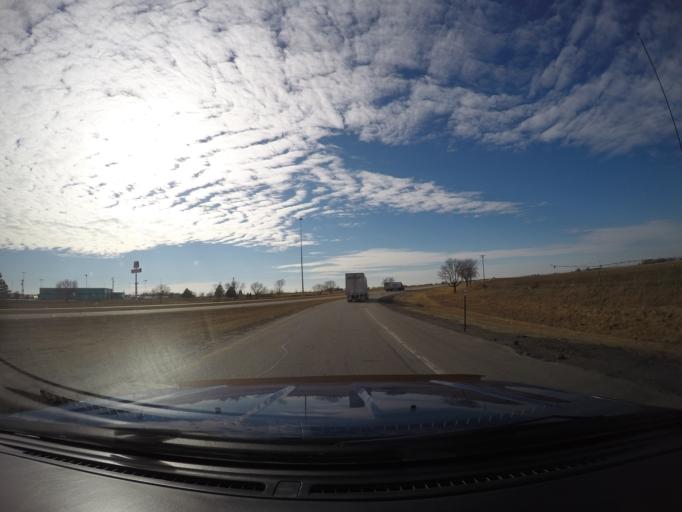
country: US
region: Nebraska
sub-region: York County
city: York
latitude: 40.8218
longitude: -97.6008
